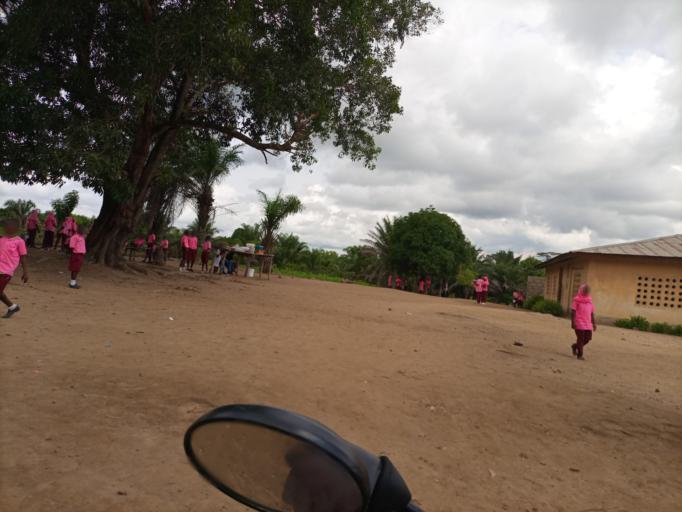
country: SL
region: Southern Province
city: Bo
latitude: 7.9730
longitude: -11.7677
